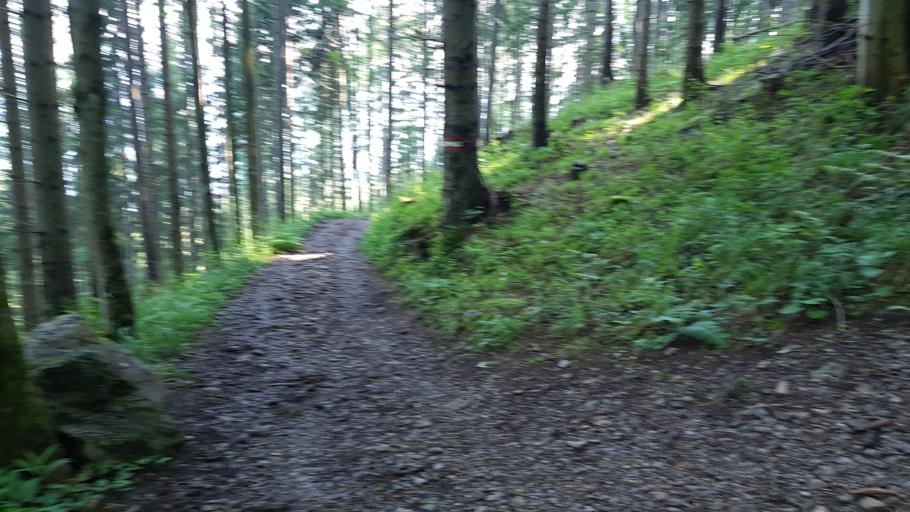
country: AT
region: Styria
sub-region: Politischer Bezirk Graz-Umgebung
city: Rothelstein
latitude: 47.3681
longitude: 15.4194
